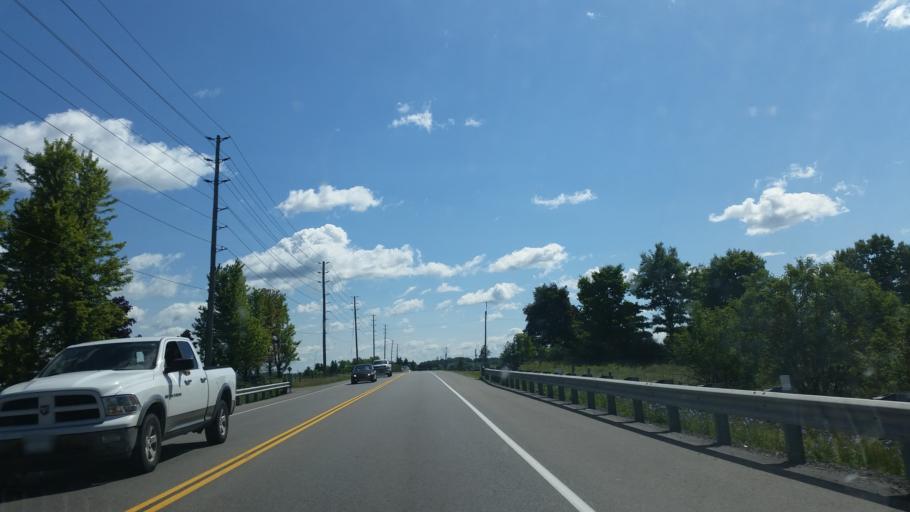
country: CA
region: Ontario
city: Brampton
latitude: 43.8903
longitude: -79.7079
